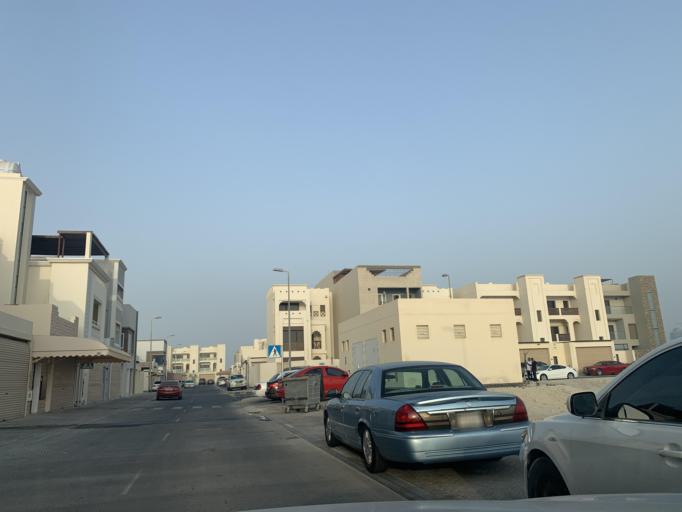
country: BH
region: Manama
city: Jidd Hafs
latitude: 26.2178
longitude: 50.4381
